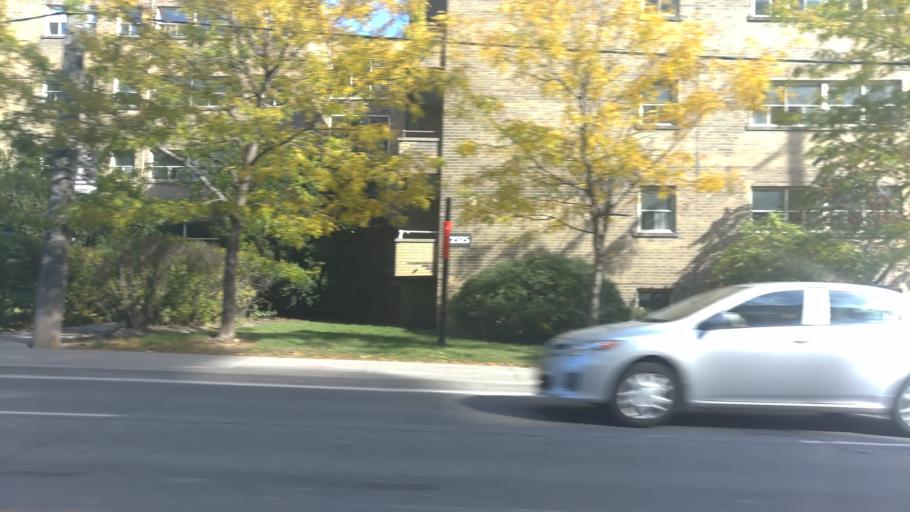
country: CA
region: Ontario
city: Toronto
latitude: 43.7059
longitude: -79.4267
